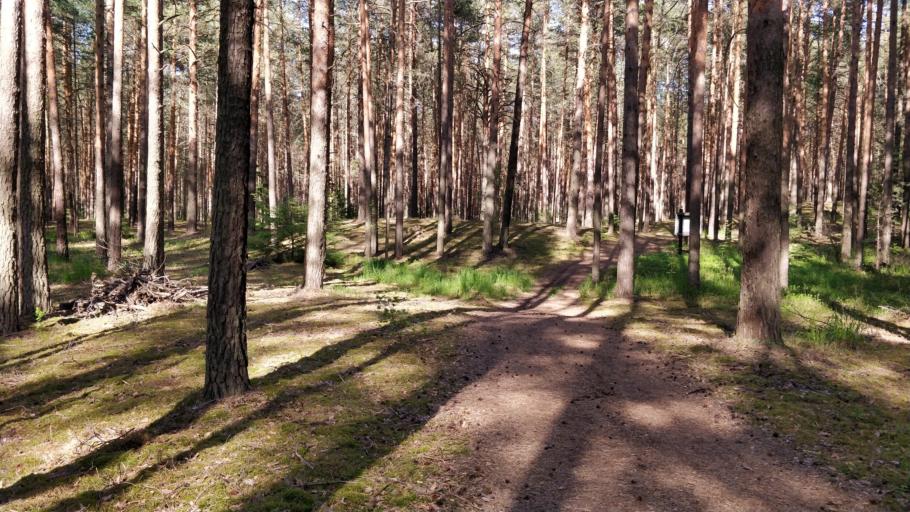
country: RU
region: Perm
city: Perm
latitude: 58.0686
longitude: 56.2865
